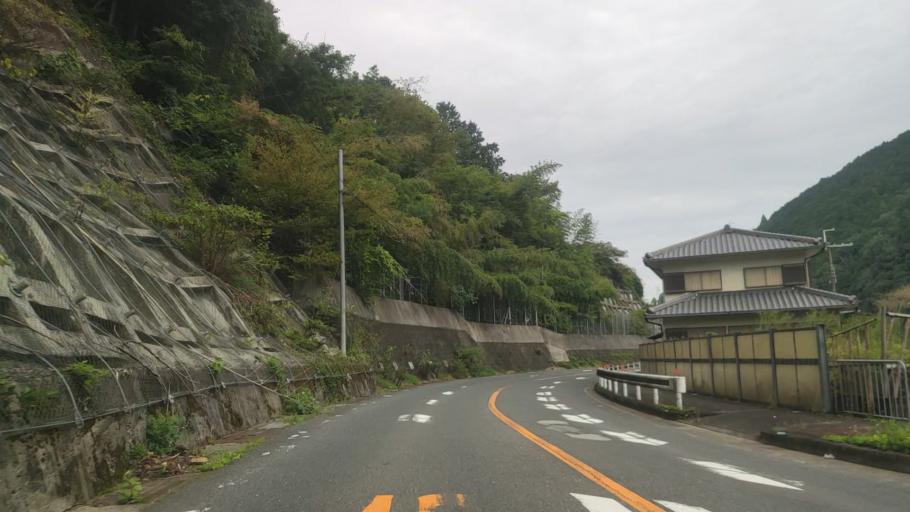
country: JP
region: Wakayama
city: Hashimoto
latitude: 34.3909
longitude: 135.5986
